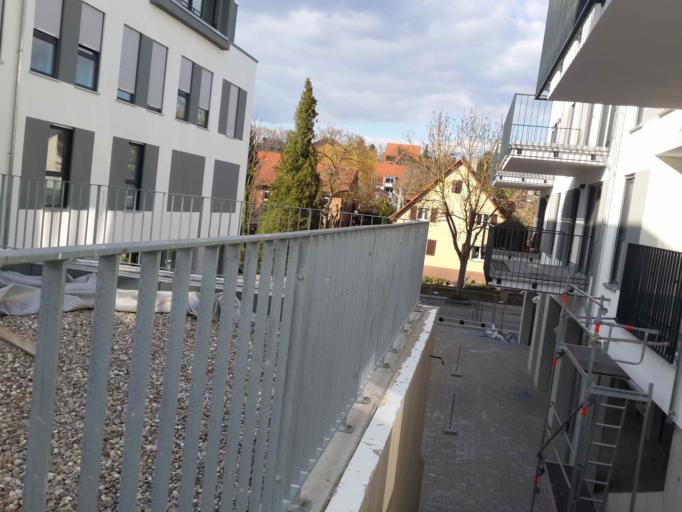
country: DE
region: Baden-Wuerttemberg
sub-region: Regierungsbezirk Stuttgart
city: Weinsberg
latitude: 49.1482
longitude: 9.2891
